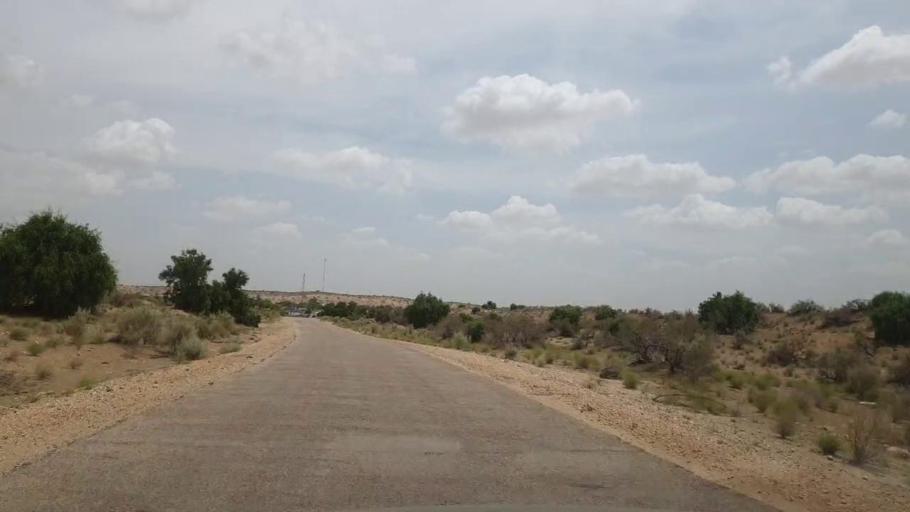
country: PK
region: Sindh
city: Kot Diji
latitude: 27.1402
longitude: 69.2251
